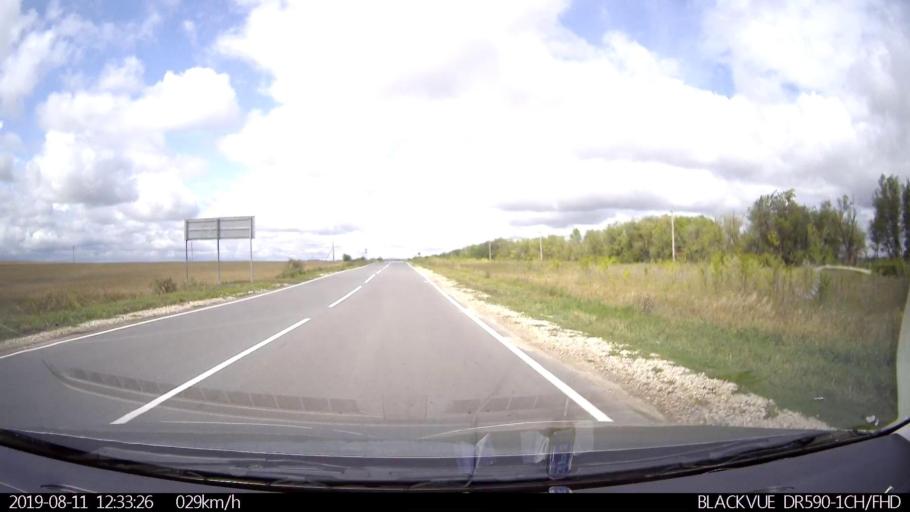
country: RU
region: Ulyanovsk
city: Ignatovka
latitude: 53.8099
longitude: 47.8551
